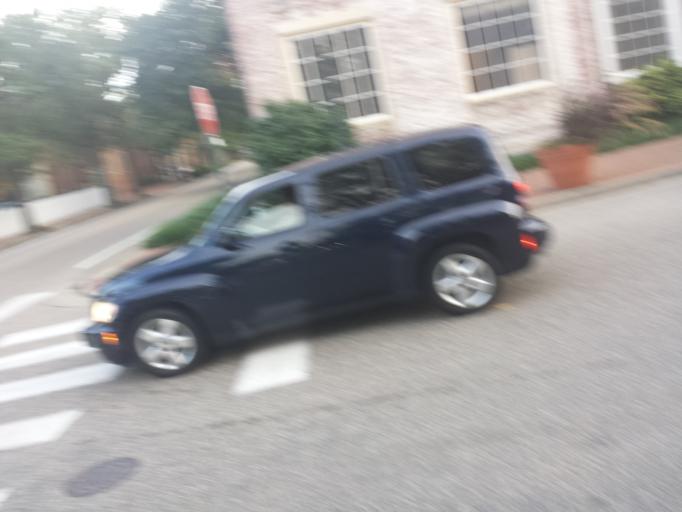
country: US
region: Virginia
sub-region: City of Williamsburg
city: Williamsburg
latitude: 37.2723
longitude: -76.7060
